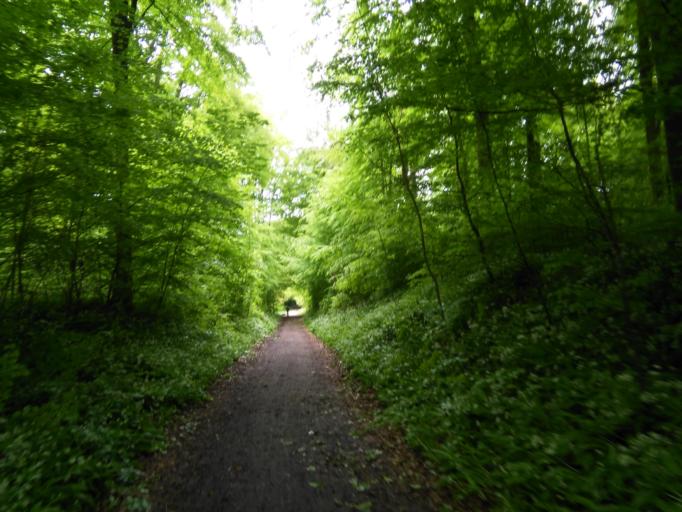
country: DK
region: Central Jutland
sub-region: Arhus Kommune
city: Arhus
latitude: 56.1781
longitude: 10.2229
